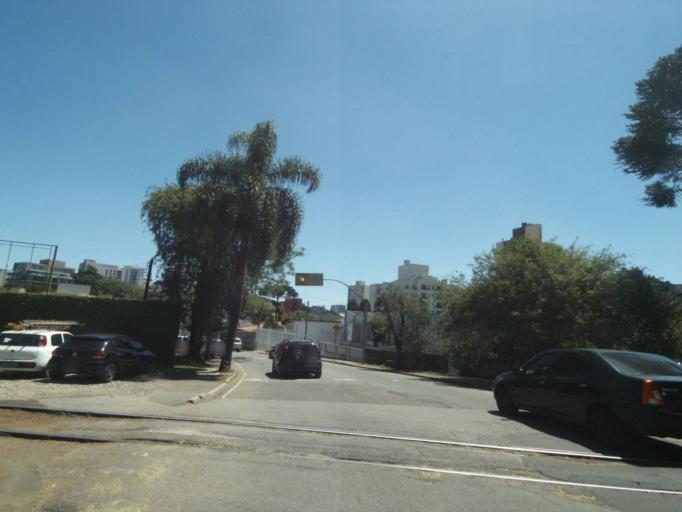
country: BR
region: Parana
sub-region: Curitiba
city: Curitiba
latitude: -25.4040
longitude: -49.2461
